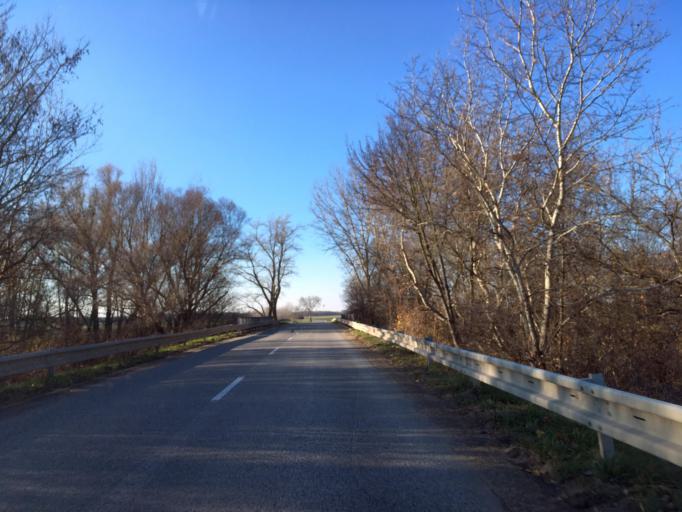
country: SK
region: Nitriansky
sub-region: Okres Komarno
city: Hurbanovo
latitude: 47.8942
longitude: 18.1871
